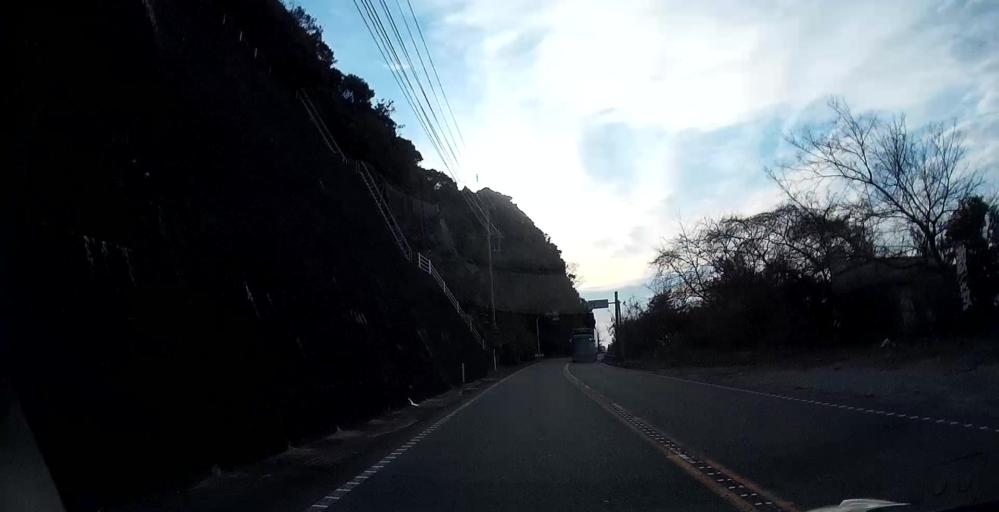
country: JP
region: Kumamoto
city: Matsubase
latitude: 32.6528
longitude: 130.4991
